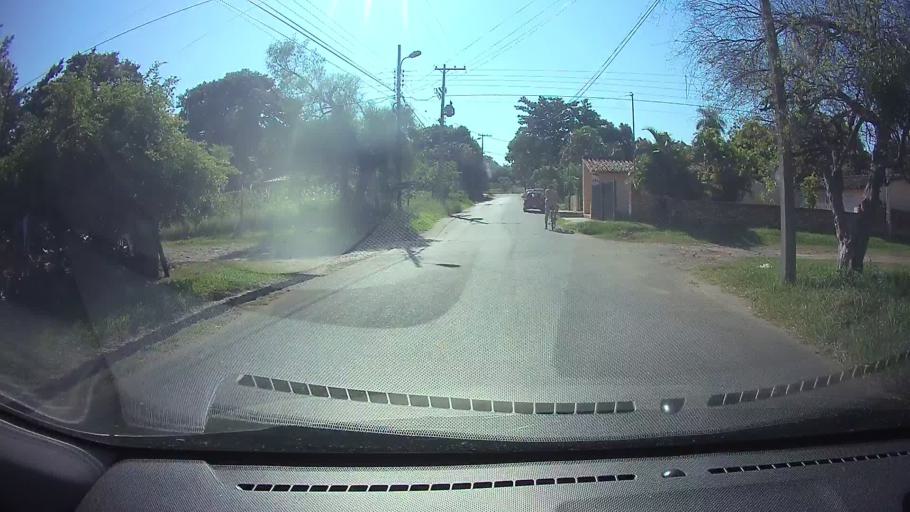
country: PY
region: Central
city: Fernando de la Mora
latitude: -25.2662
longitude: -57.5176
